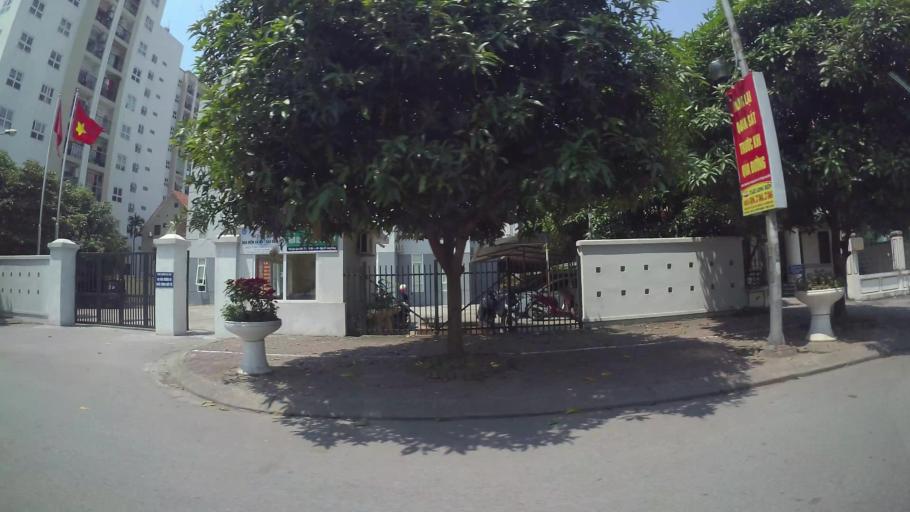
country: VN
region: Ha Noi
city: Hoan Kiem
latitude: 21.0487
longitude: 105.8848
